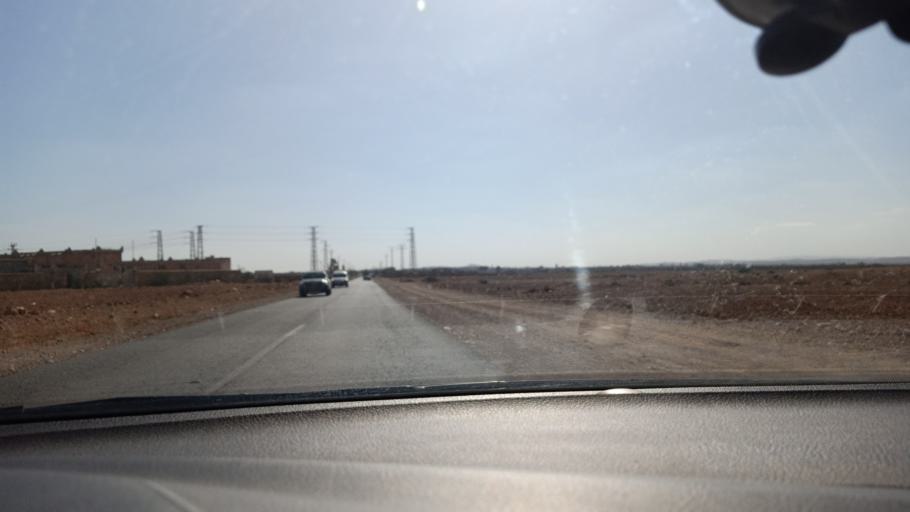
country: MA
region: Doukkala-Abda
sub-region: Safi
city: Youssoufia
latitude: 32.1118
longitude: -8.6079
